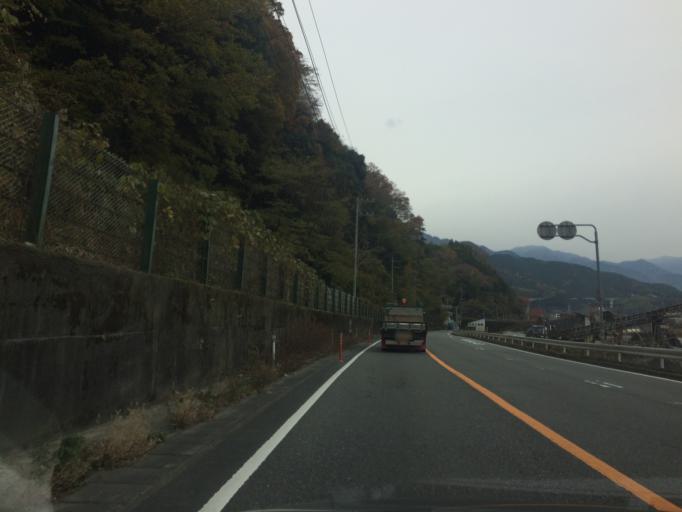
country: JP
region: Shizuoka
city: Fujinomiya
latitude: 35.2374
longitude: 138.4926
